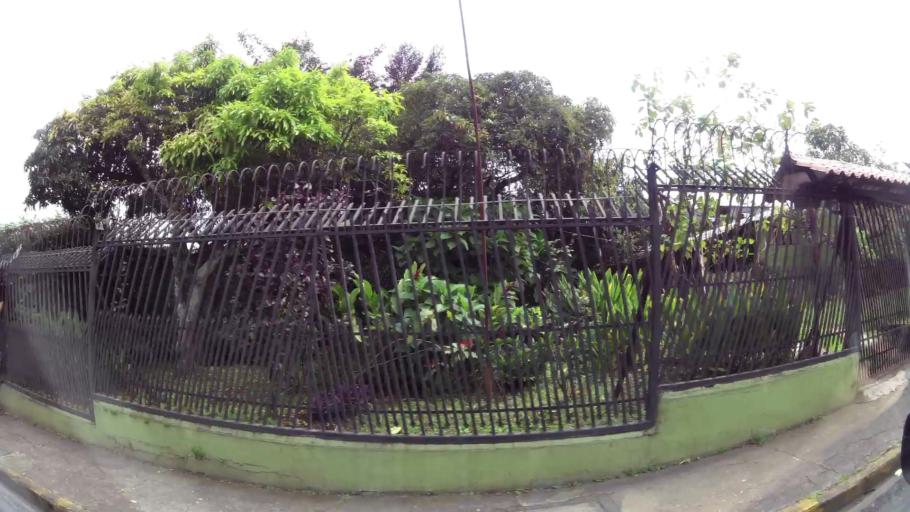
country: CR
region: San Jose
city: San Rafael Arriba
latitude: 9.8960
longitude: -84.0653
